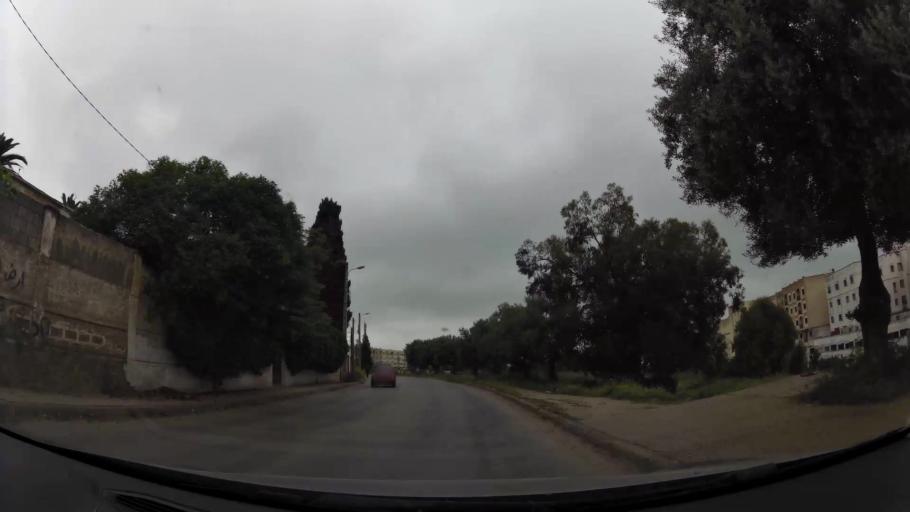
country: MA
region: Fes-Boulemane
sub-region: Fes
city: Fes
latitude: 34.0331
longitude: -4.9916
